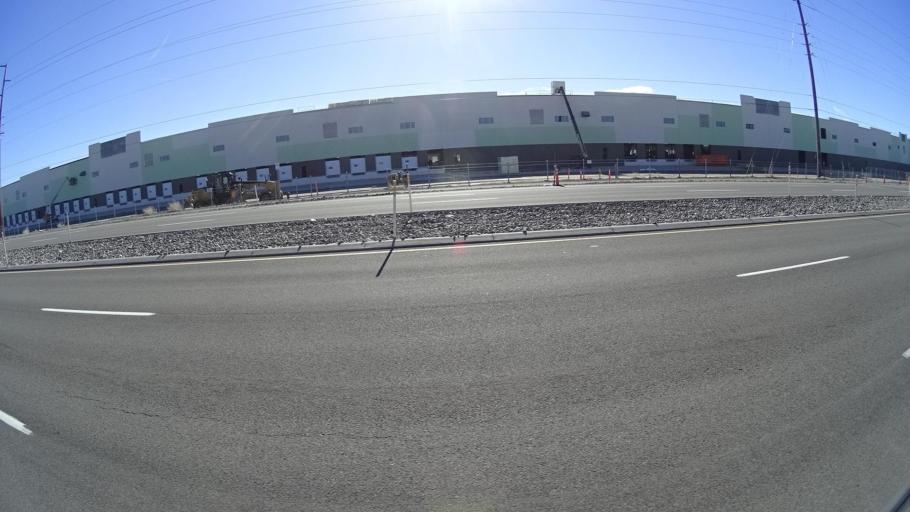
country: US
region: Nevada
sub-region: Washoe County
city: Sparks
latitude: 39.5068
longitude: -119.7477
